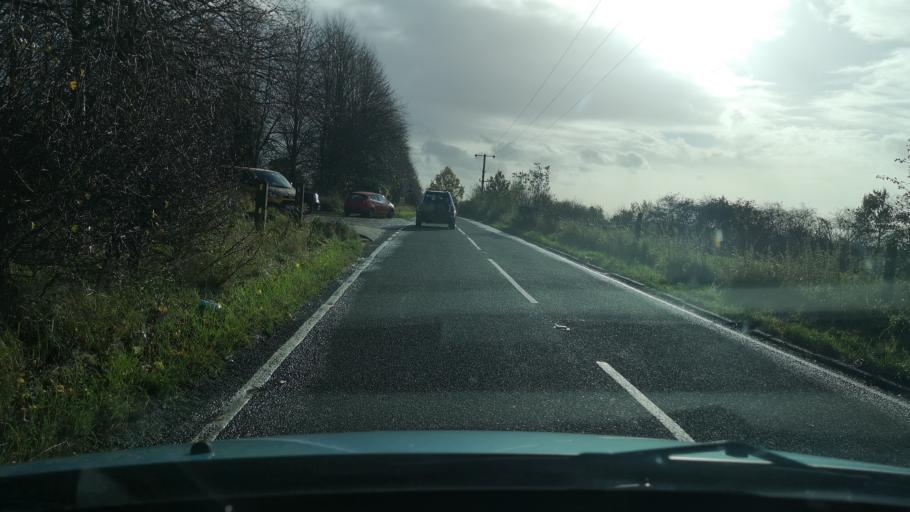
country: GB
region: England
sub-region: City and Borough of Wakefield
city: Crofton
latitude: 53.6472
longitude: -1.4194
